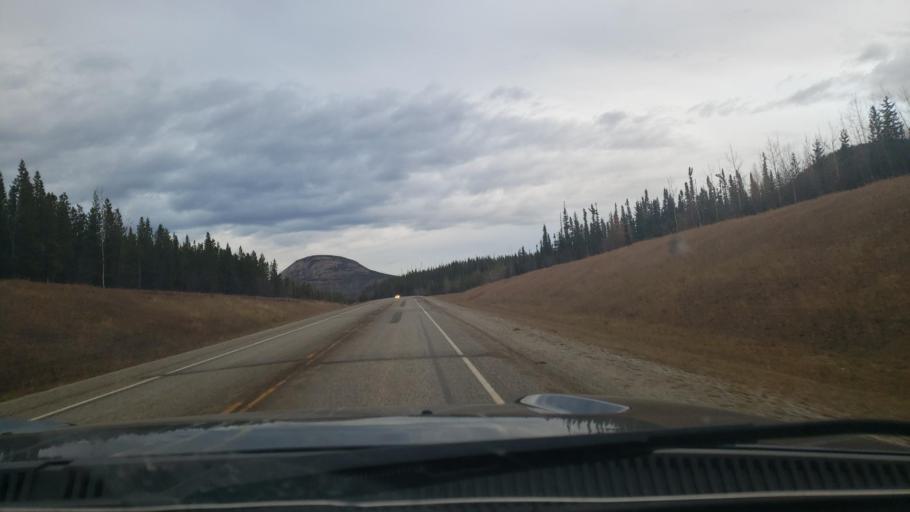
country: CA
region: Yukon
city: Watson Lake
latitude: 59.9067
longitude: -127.4360
